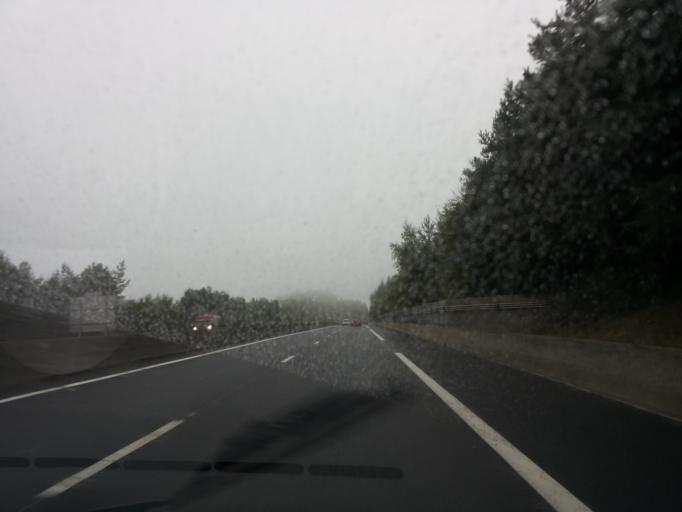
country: FR
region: Lorraine
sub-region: Departement des Vosges
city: Epinal
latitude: 48.1678
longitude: 6.4856
